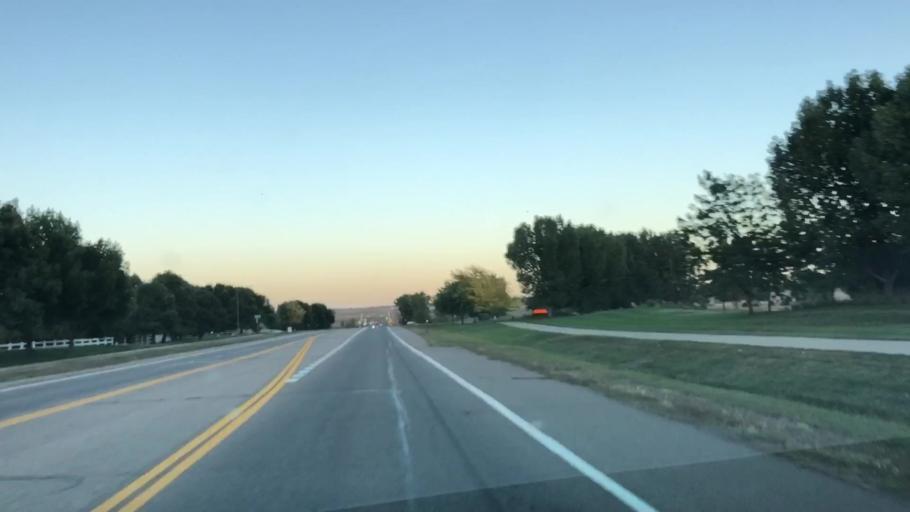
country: US
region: Colorado
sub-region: Larimer County
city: Loveland
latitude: 40.4802
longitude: -105.0468
